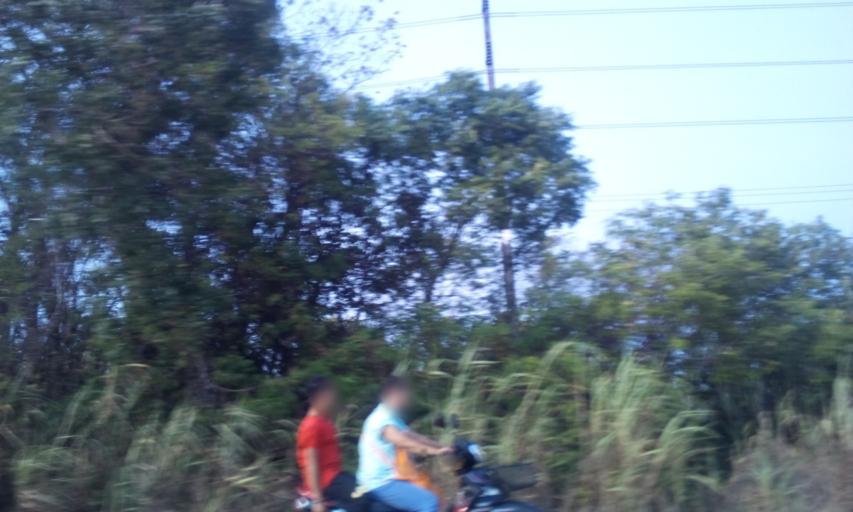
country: TH
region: Chanthaburi
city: Khlung
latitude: 12.4576
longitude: 102.2343
